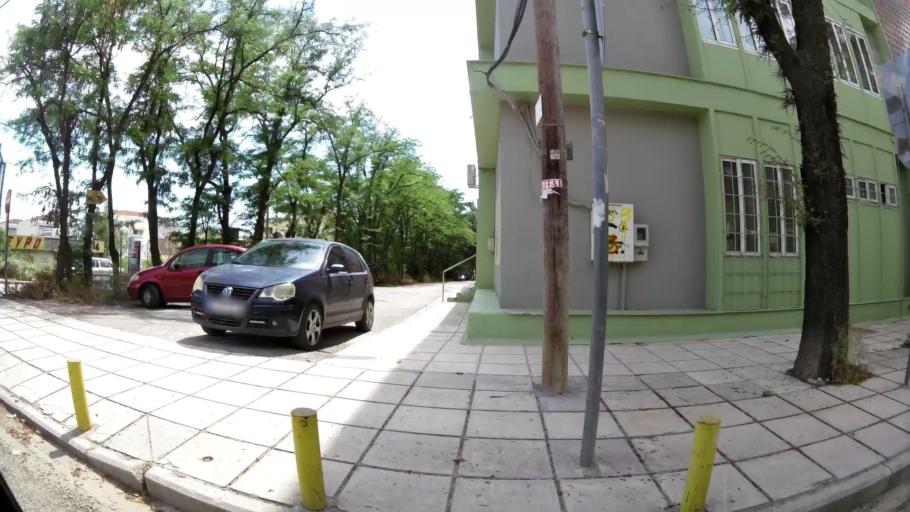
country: GR
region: Central Macedonia
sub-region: Nomos Thessalonikis
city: Pylaia
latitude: 40.5957
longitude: 22.9752
